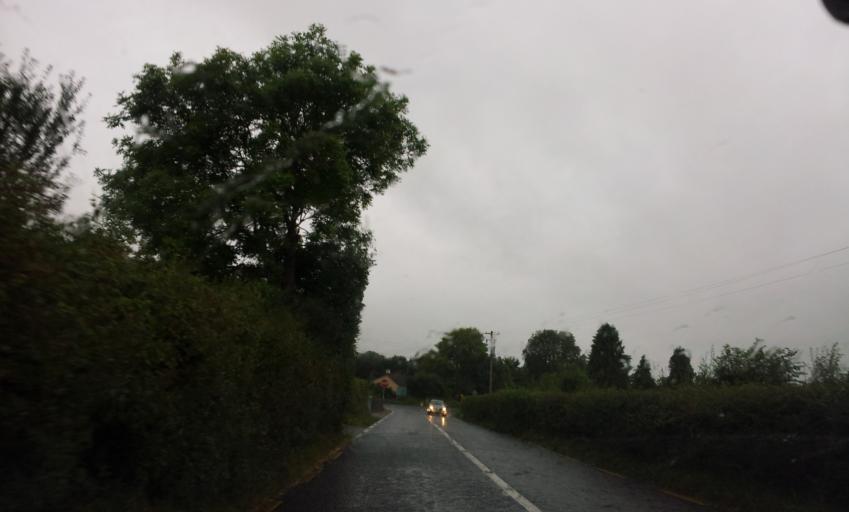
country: IE
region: Munster
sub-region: County Cork
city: Mallow
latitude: 52.1497
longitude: -8.6145
